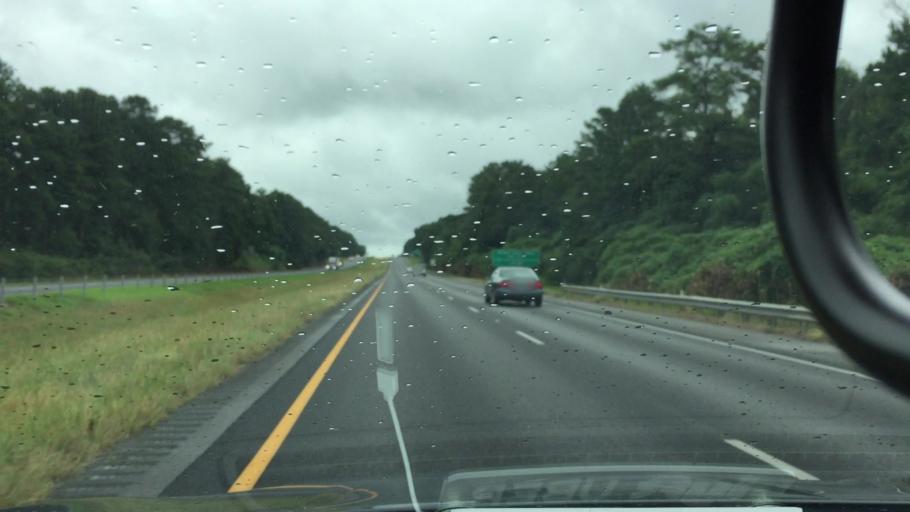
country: US
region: Alabama
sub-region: Lee County
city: Opelika
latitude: 32.6089
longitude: -85.4194
